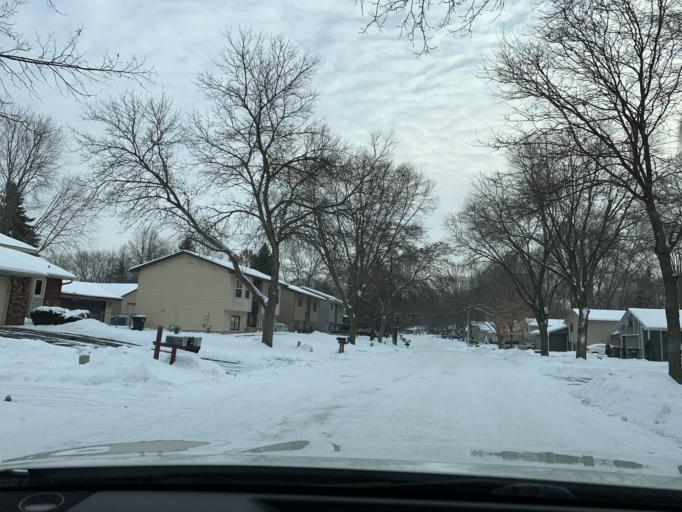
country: US
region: Minnesota
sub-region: Anoka County
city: Coon Rapids
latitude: 45.1593
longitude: -93.2915
